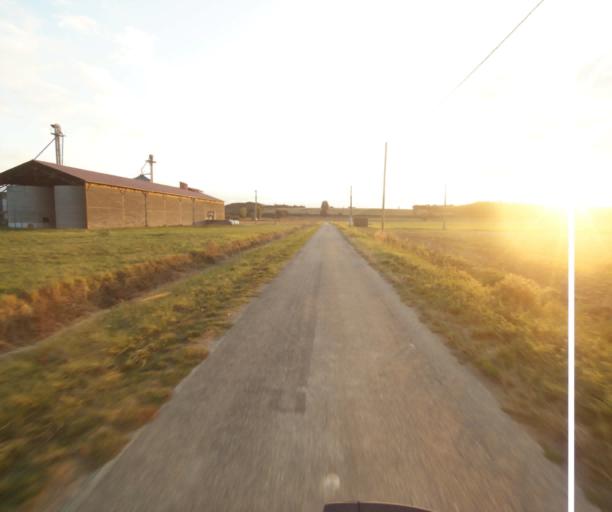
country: FR
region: Midi-Pyrenees
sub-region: Departement du Tarn-et-Garonne
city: Verdun-sur-Garonne
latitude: 43.8309
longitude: 1.2150
